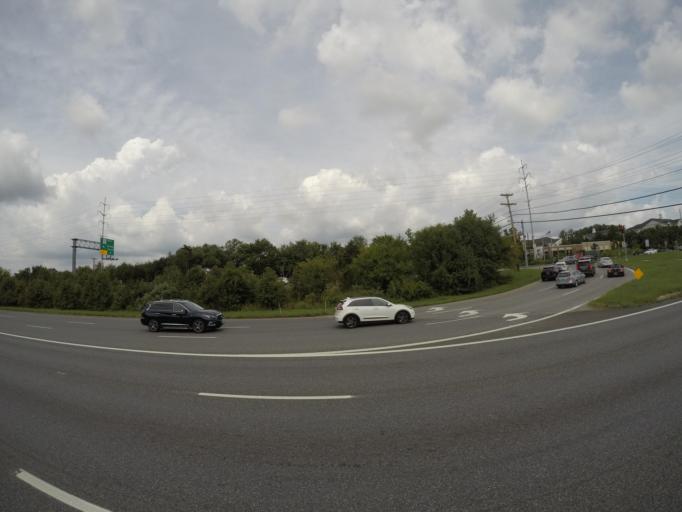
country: US
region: Maryland
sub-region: Anne Arundel County
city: Gambrills
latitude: 39.0385
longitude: -76.6750
